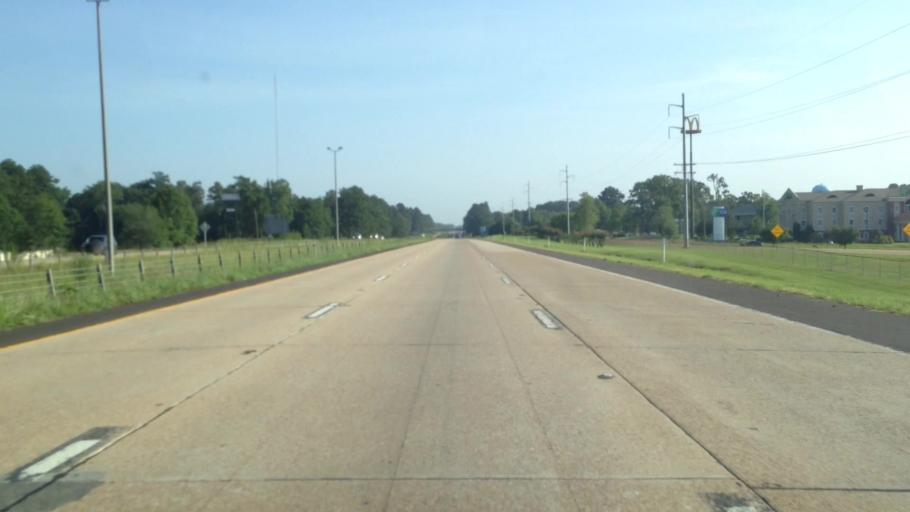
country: US
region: Mississippi
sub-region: Pike County
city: Summit
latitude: 31.2624
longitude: -90.4790
